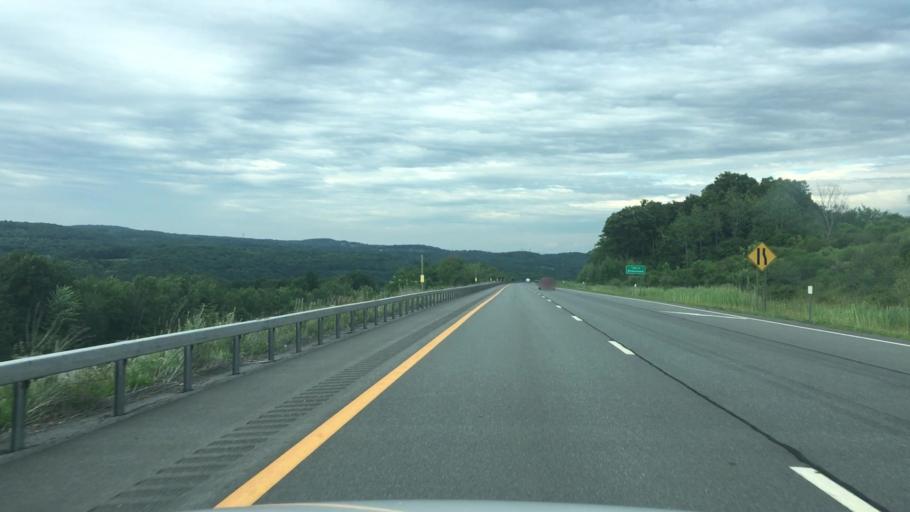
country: US
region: New York
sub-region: Albany County
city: Altamont
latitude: 42.7673
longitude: -74.1015
